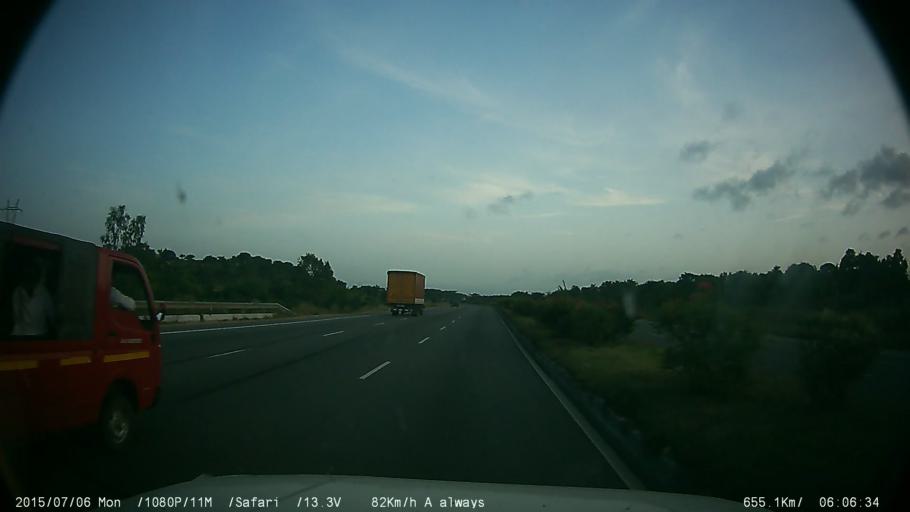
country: IN
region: Tamil Nadu
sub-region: Krishnagiri
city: Krishnagiri
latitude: 12.6334
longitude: 78.0728
